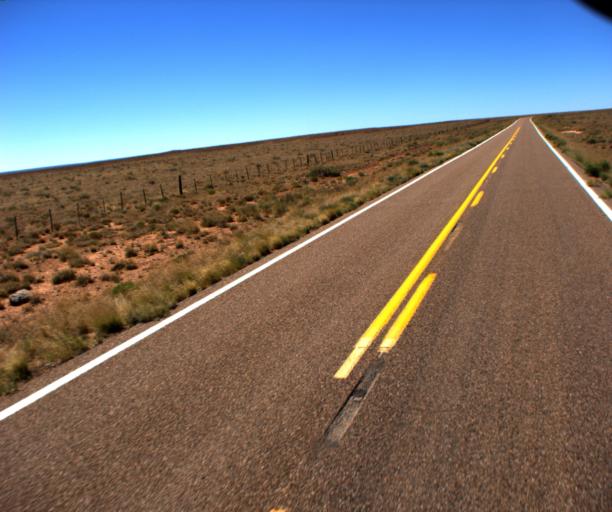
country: US
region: Arizona
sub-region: Navajo County
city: Winslow
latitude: 34.9204
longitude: -110.6378
